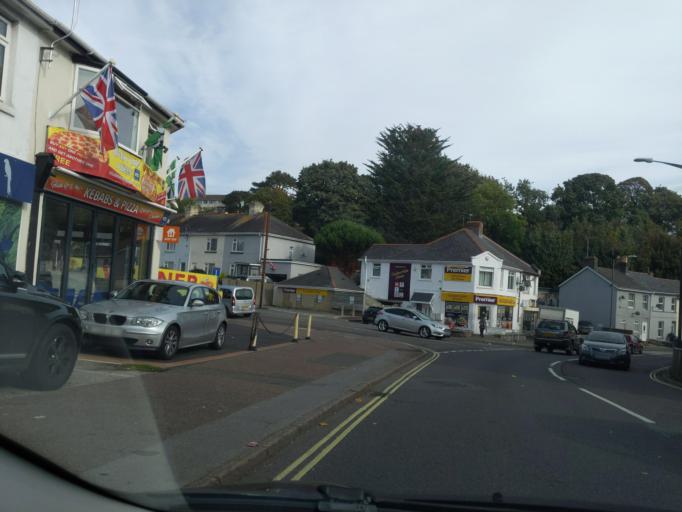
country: GB
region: England
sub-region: Borough of Torbay
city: Torquay
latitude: 50.4851
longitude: -3.5402
